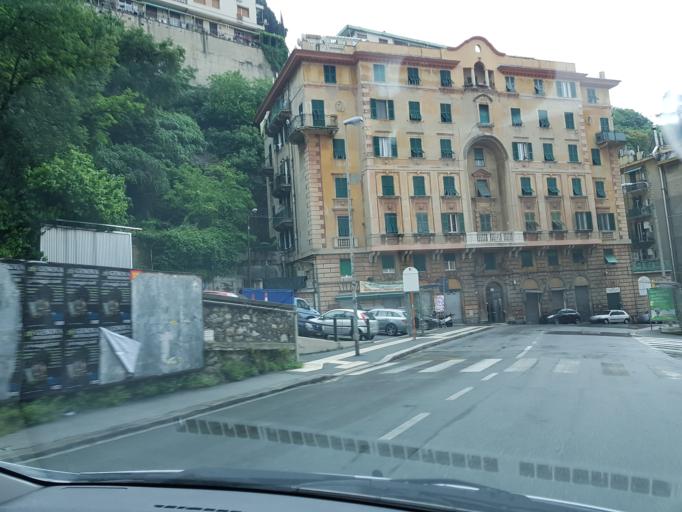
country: IT
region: Liguria
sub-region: Provincia di Genova
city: San Teodoro
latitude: 44.4179
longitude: 8.9100
